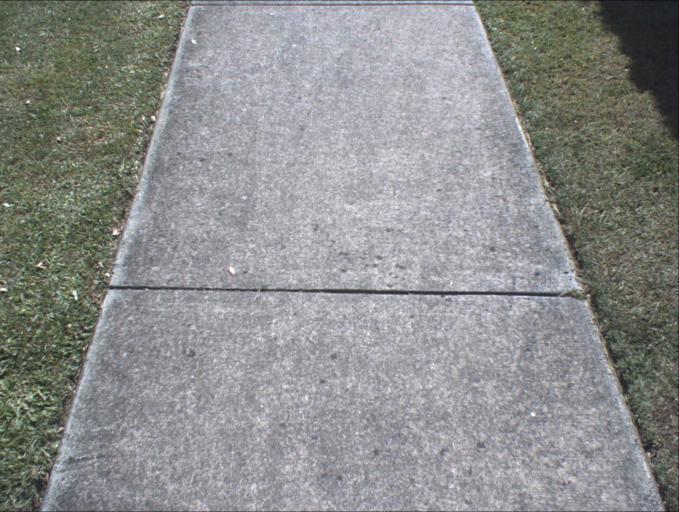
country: AU
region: Queensland
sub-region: Logan
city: Logan City
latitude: -27.6458
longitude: 153.1015
